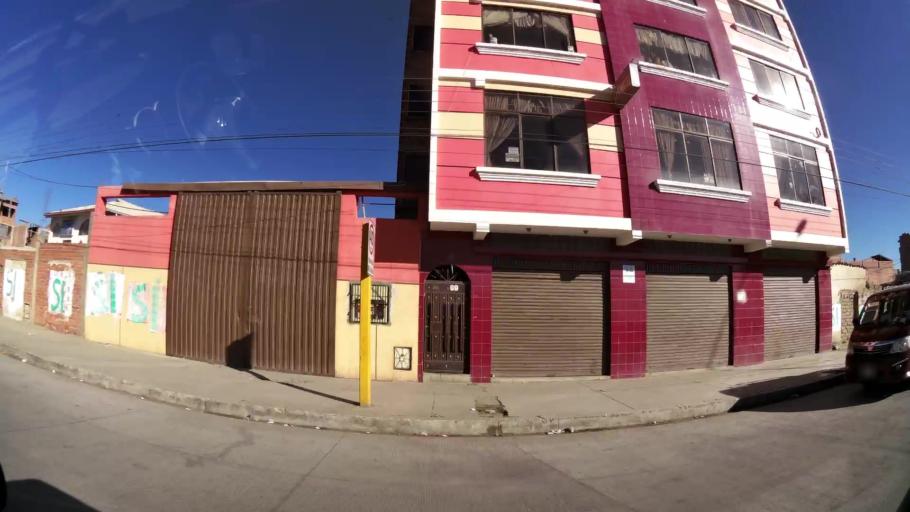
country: BO
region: La Paz
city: La Paz
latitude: -16.5226
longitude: -68.1582
